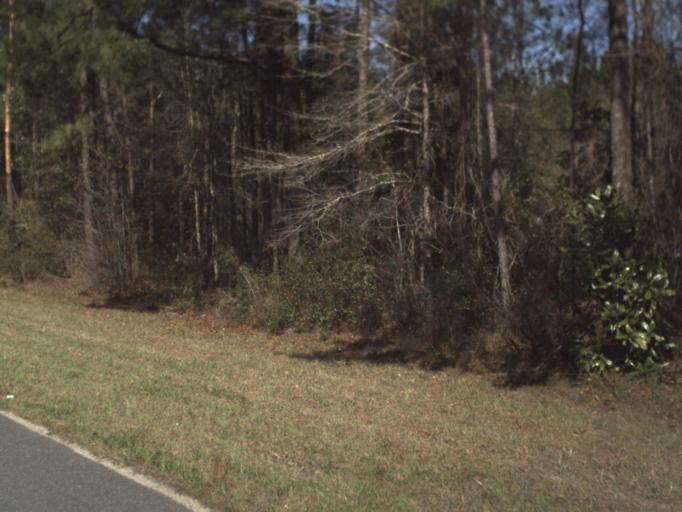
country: US
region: Florida
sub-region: Jackson County
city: Marianna
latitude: 30.7413
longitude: -85.1487
